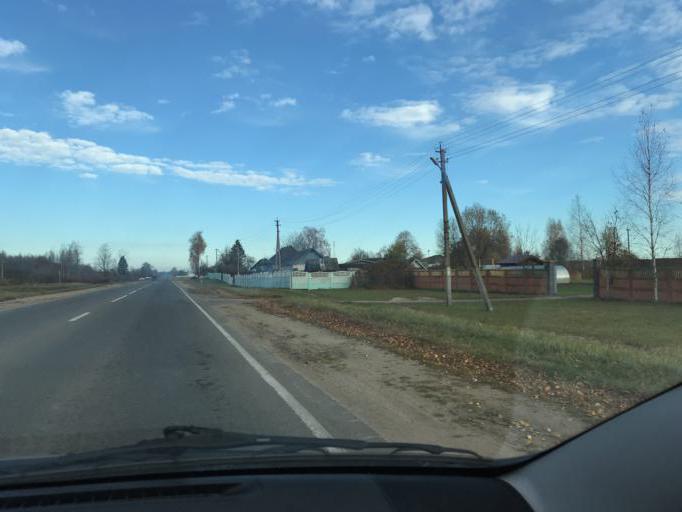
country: BY
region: Vitebsk
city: Haradok
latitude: 55.4774
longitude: 29.9690
